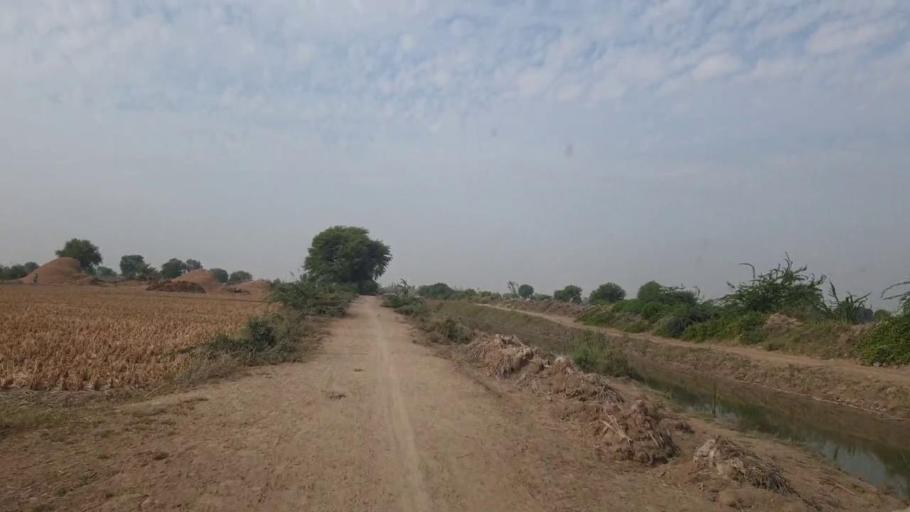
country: PK
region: Sindh
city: Talhar
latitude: 24.8789
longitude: 68.9148
